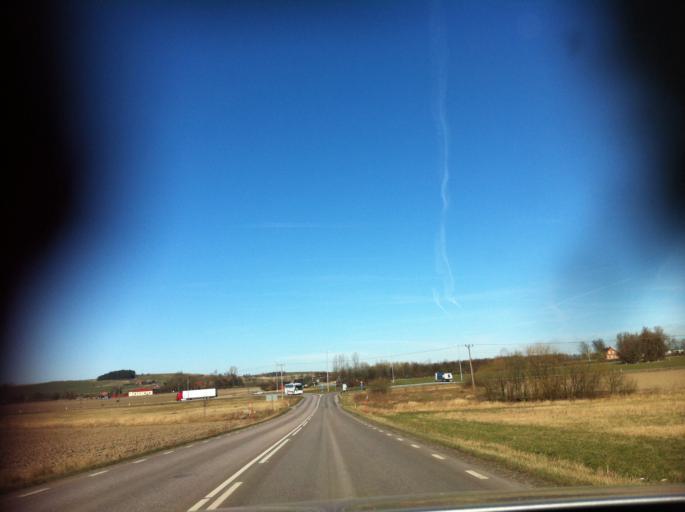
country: SE
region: Skane
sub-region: Landskrona
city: Asmundtorp
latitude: 55.8891
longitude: 12.9662
